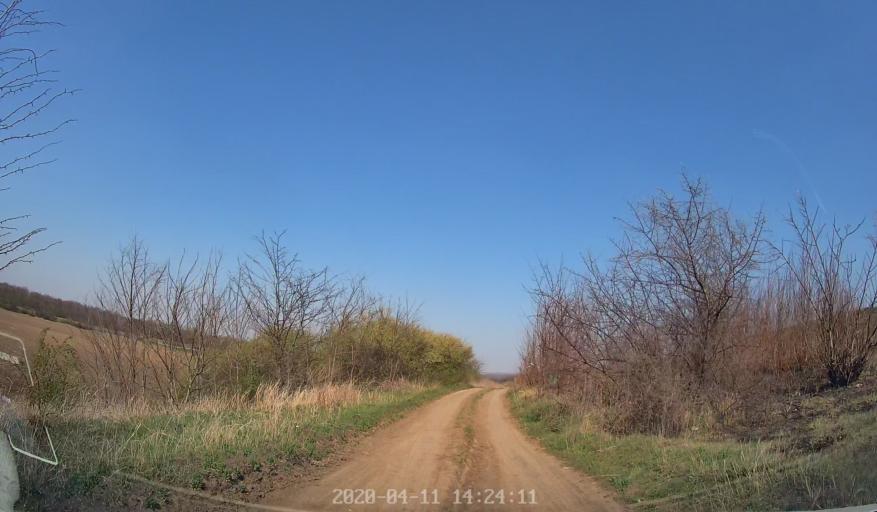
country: MD
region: Chisinau
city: Vadul lui Voda
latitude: 47.0913
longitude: 29.1416
